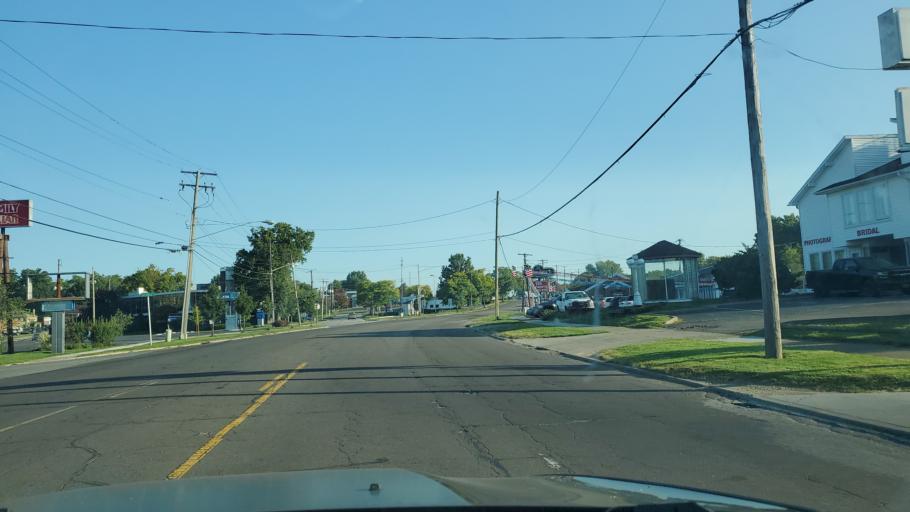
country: US
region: Ohio
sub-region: Mahoning County
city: Boardman
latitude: 41.0583
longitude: -80.6628
